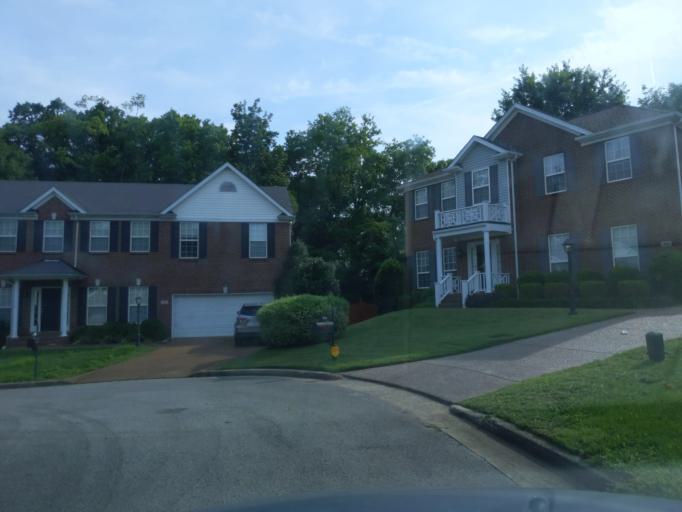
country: US
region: Tennessee
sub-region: Williamson County
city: Brentwood Estates
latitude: 36.0252
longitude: -86.7515
